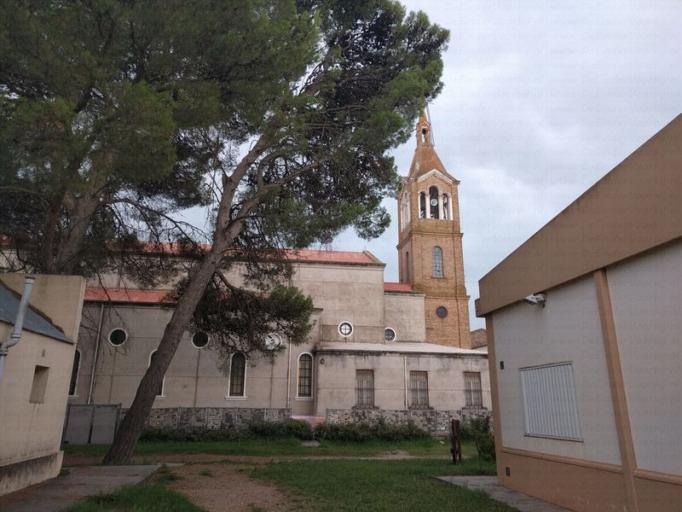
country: AR
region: Buenos Aires
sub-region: Partido de Villarino
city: Medanos
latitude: -39.5248
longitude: -62.6612
